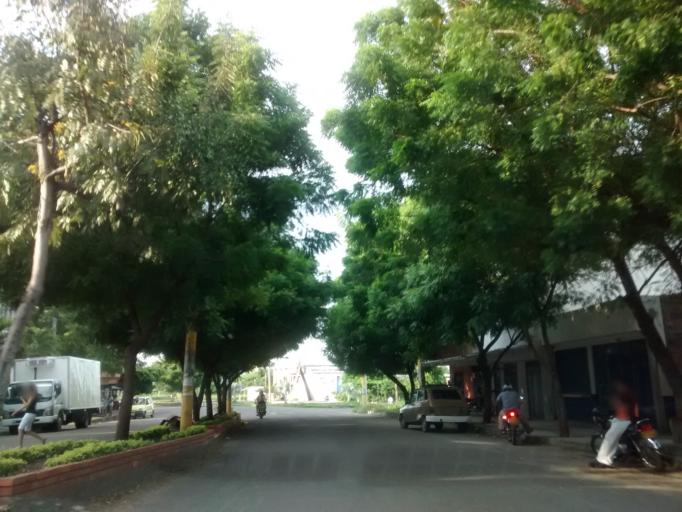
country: CO
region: Cundinamarca
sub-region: Girardot
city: Girardot City
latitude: 4.3066
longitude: -74.8061
